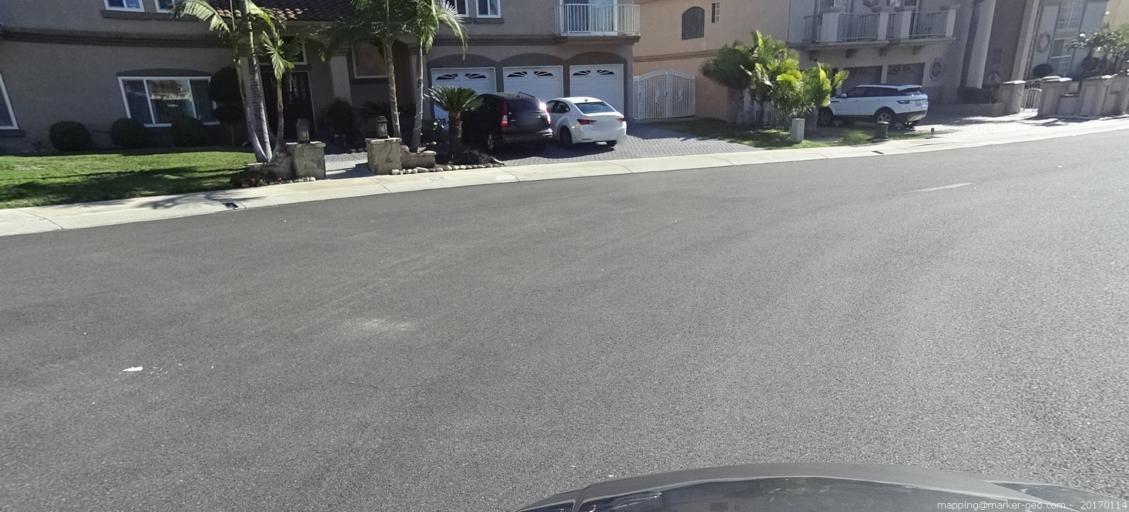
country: US
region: California
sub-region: Orange County
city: North Tustin
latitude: 33.7730
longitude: -117.8025
